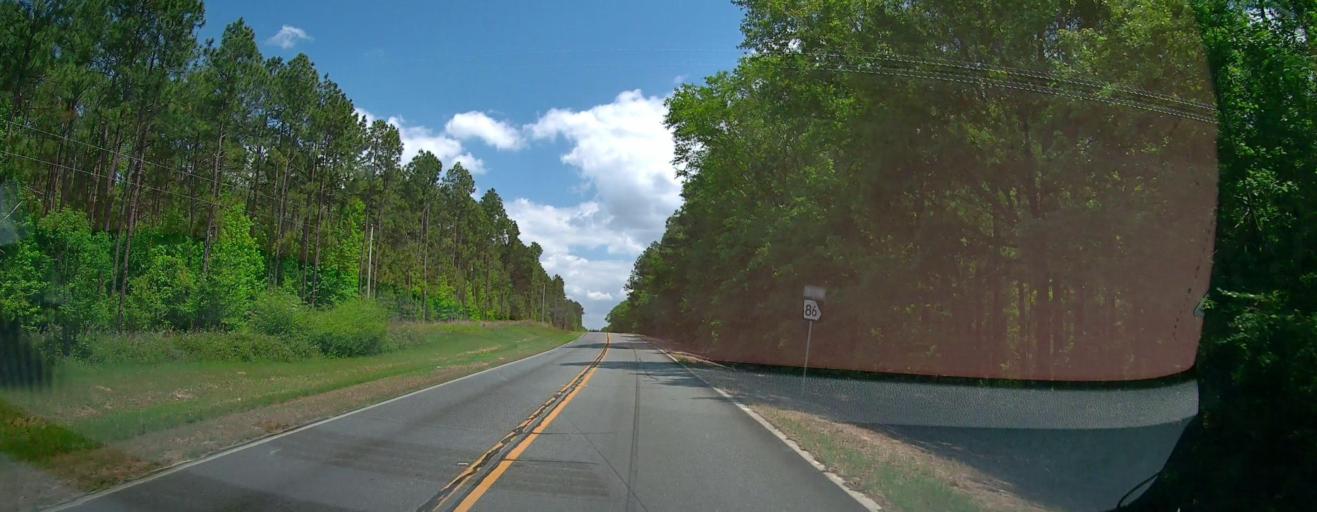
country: US
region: Georgia
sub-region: Treutlen County
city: Soperton
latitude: 32.5092
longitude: -82.6398
